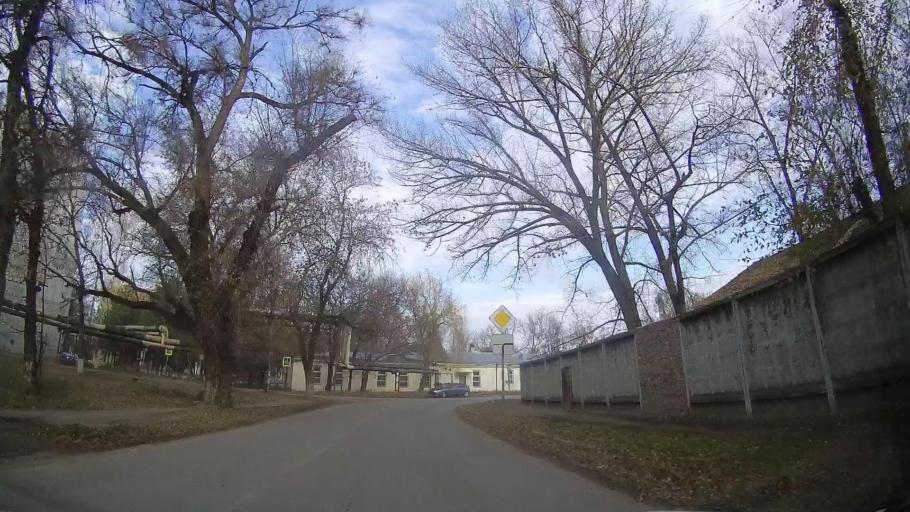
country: RU
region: Rostov
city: Bataysk
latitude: 47.1275
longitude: 39.7832
